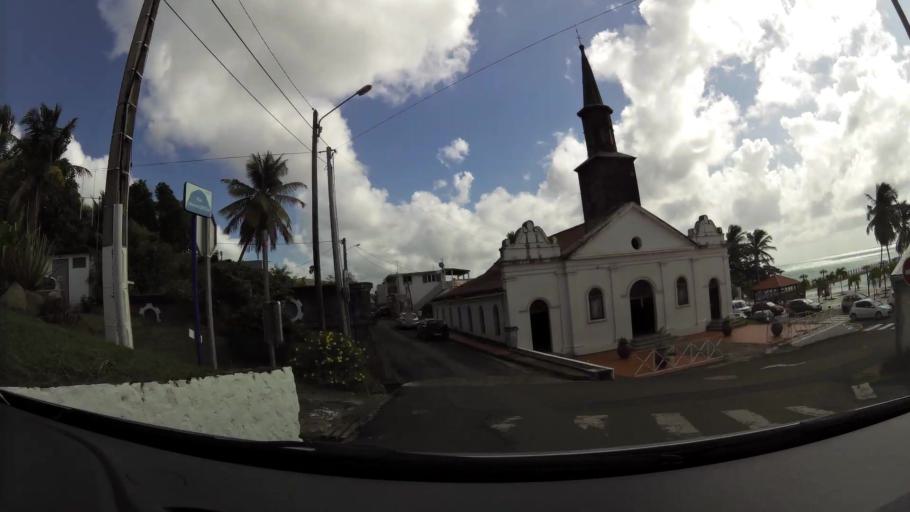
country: MQ
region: Martinique
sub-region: Martinique
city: Les Trois-Ilets
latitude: 14.4800
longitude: -61.0264
